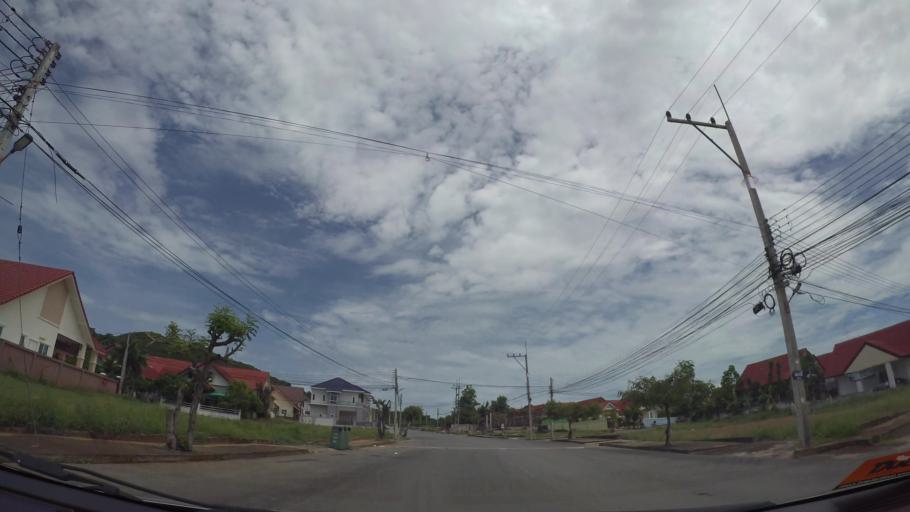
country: TH
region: Chon Buri
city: Sattahip
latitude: 12.6891
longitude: 100.8870
